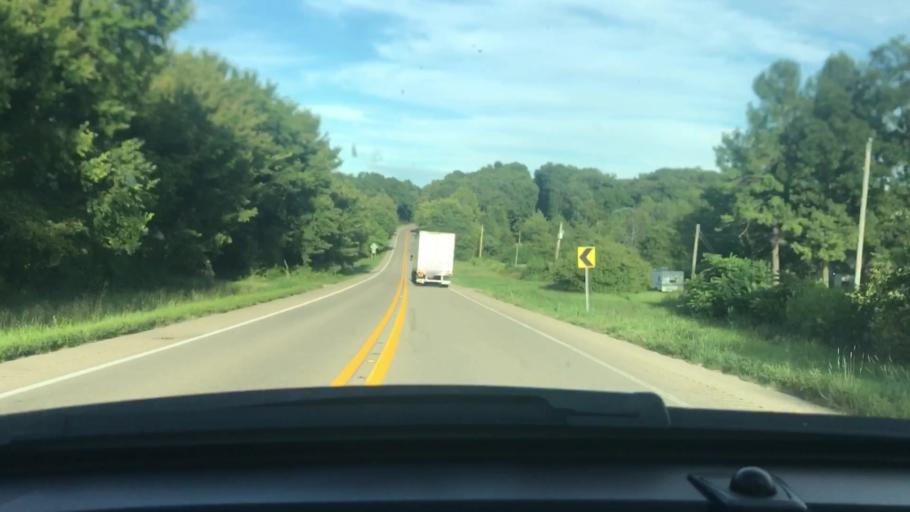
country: US
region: Arkansas
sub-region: Randolph County
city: Pocahontas
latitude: 36.2124
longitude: -91.2113
